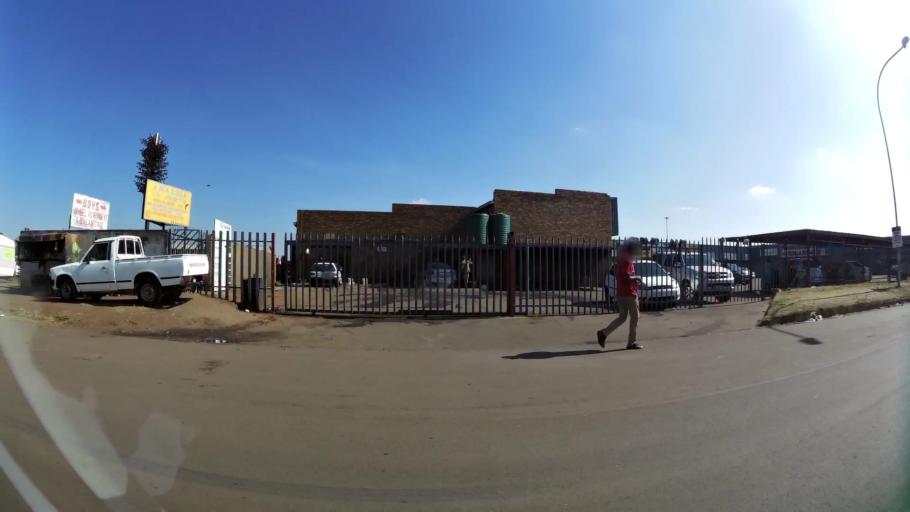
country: ZA
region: Gauteng
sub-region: City of Johannesburg Metropolitan Municipality
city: Soweto
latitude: -26.2902
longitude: 27.8503
